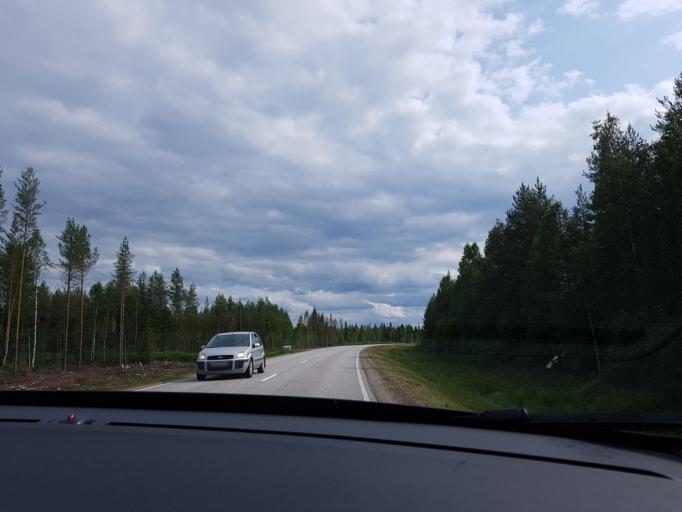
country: FI
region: Kainuu
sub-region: Kehys-Kainuu
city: Kuhmo
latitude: 64.3699
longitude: 29.8907
